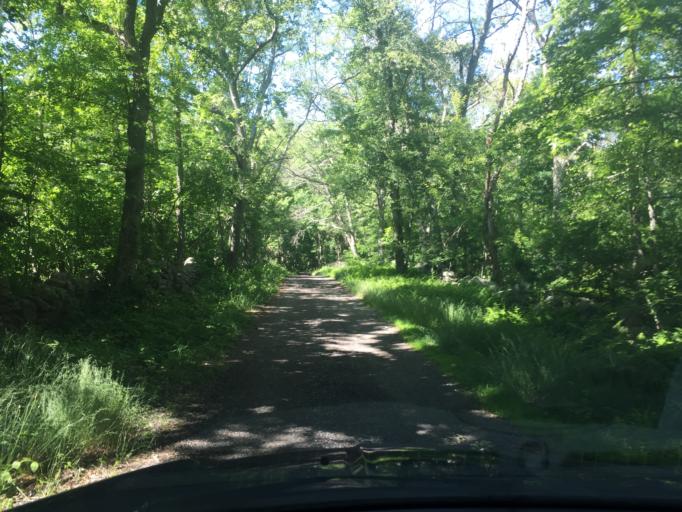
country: US
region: Rhode Island
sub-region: Washington County
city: Hopkinton
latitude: 41.5129
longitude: -71.8015
